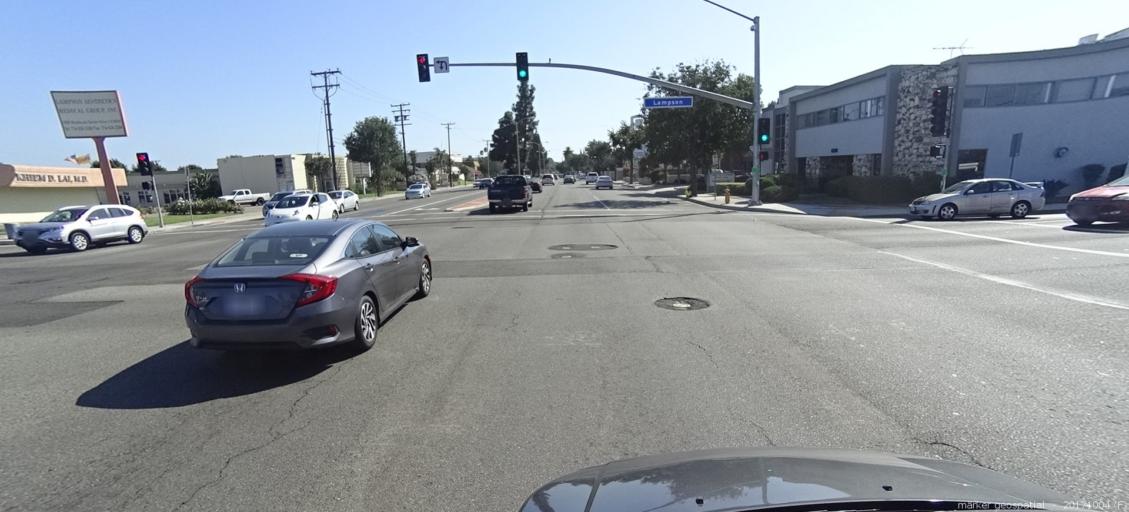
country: US
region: California
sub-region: Orange County
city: Garden Grove
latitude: 33.7815
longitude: -117.9587
